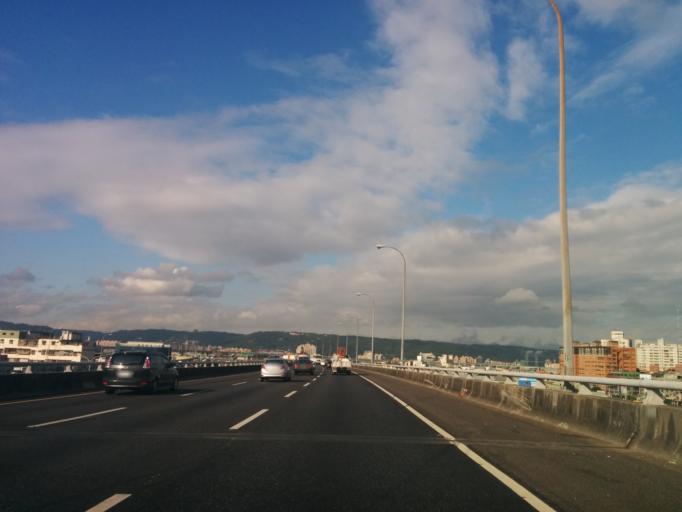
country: TW
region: Taipei
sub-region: Taipei
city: Banqiao
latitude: 25.0761
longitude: 121.4683
